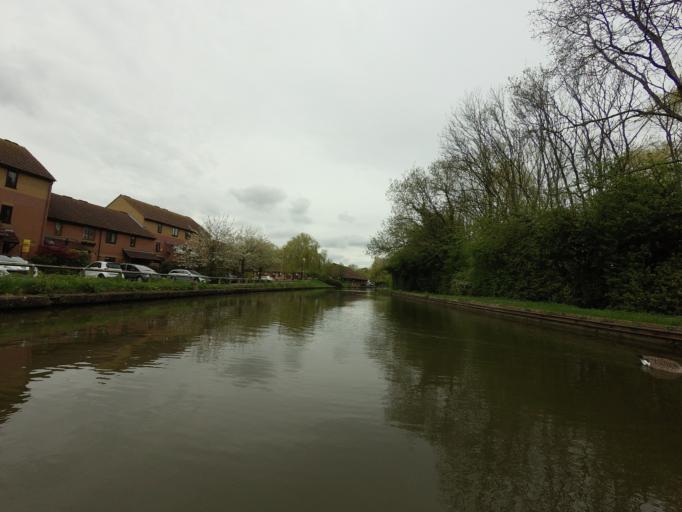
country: GB
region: England
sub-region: Milton Keynes
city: Milton Keynes
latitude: 52.0270
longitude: -0.7300
